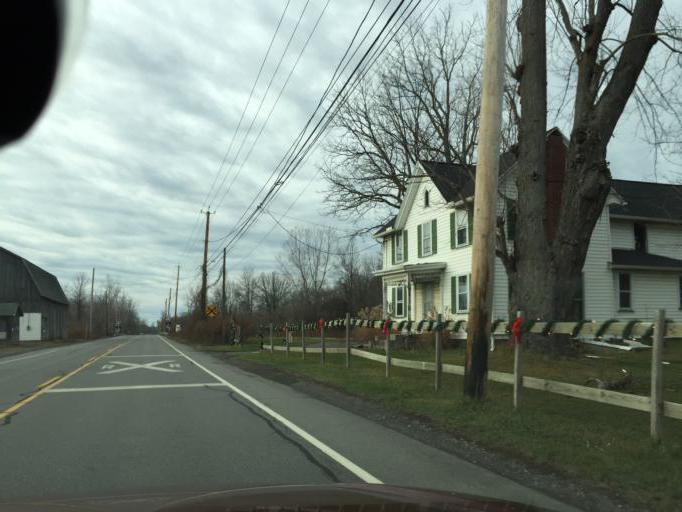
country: US
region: New York
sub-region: Monroe County
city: Scottsville
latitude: 43.0927
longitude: -77.7048
